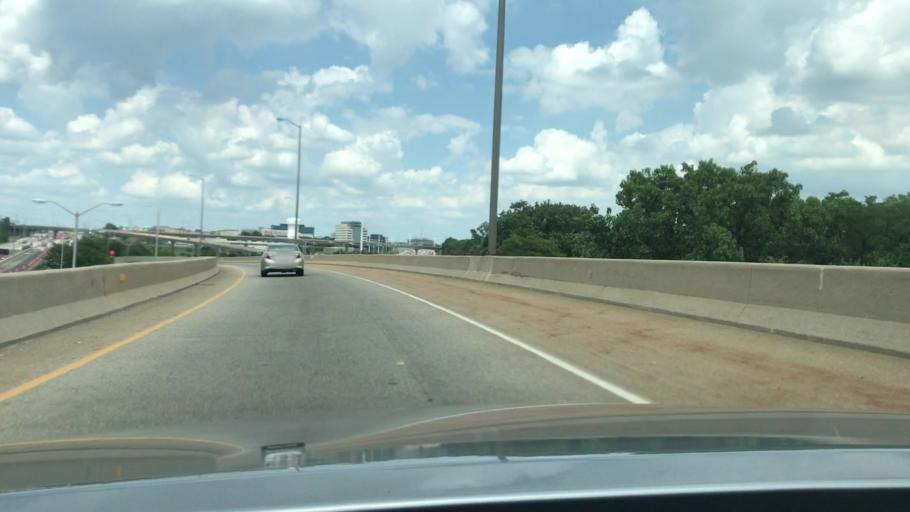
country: US
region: Illinois
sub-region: DuPage County
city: Downers Grove
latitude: 41.8143
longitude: -88.0277
